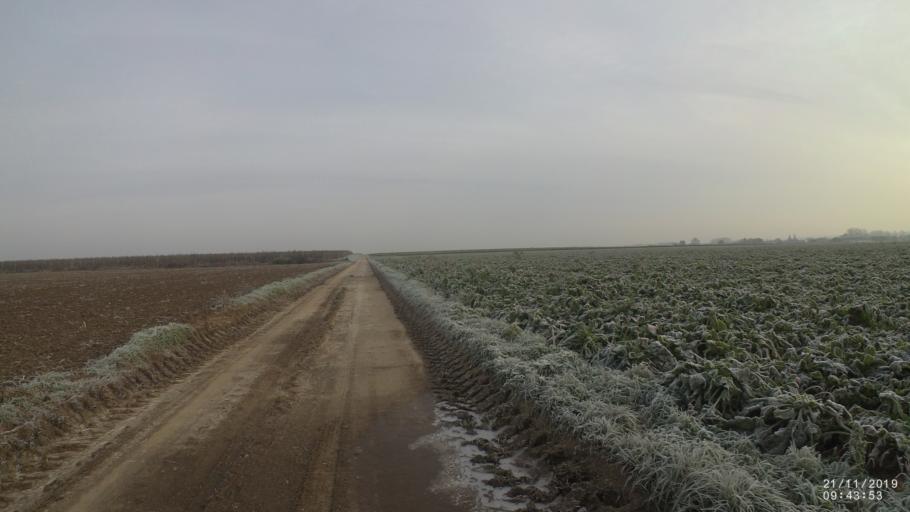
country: BE
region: Flanders
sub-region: Provincie Vlaams-Brabant
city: Tienen
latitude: 50.7854
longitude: 4.9963
